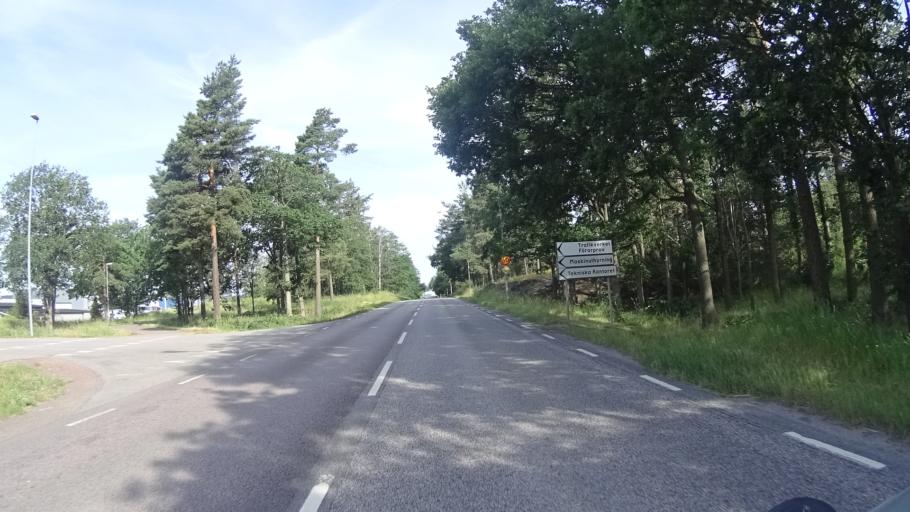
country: SE
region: Kalmar
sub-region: Oskarshamns Kommun
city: Oskarshamn
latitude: 57.2539
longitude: 16.4417
